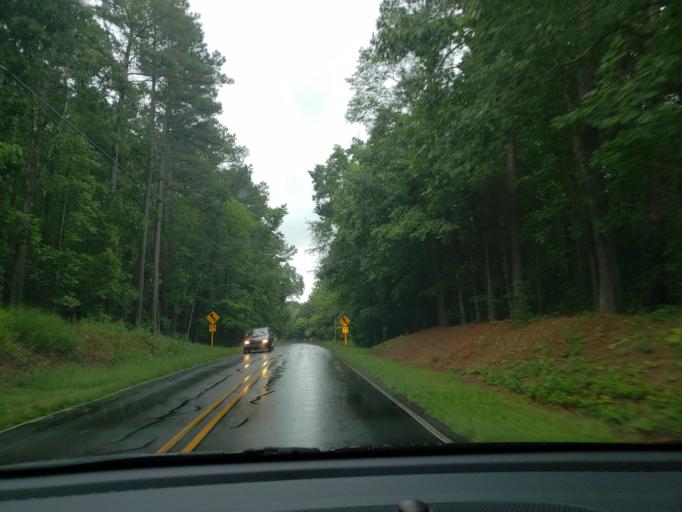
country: US
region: North Carolina
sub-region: Orange County
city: Chapel Hill
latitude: 35.9946
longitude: -79.0083
